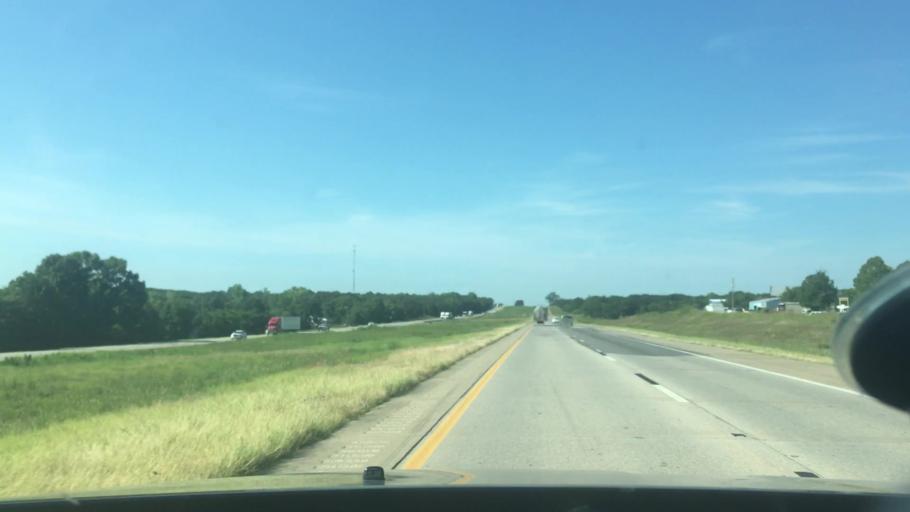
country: US
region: Oklahoma
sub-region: Atoka County
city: Atoka
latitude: 34.1907
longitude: -96.2435
